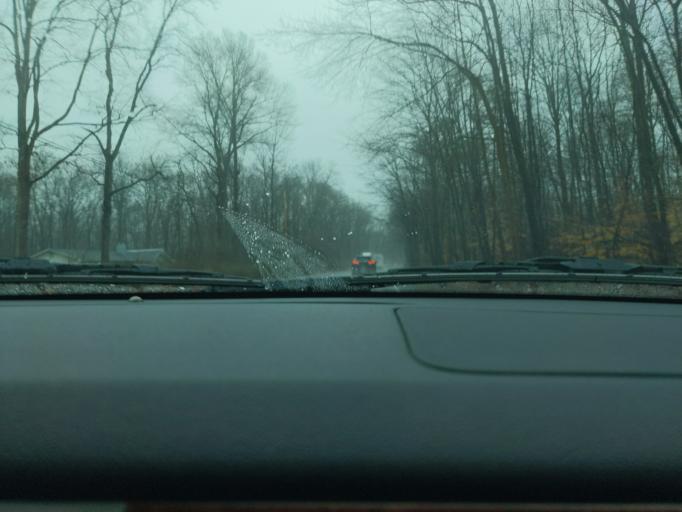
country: US
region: Pennsylvania
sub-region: Bucks County
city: Perkasie
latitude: 40.4264
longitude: -75.2848
